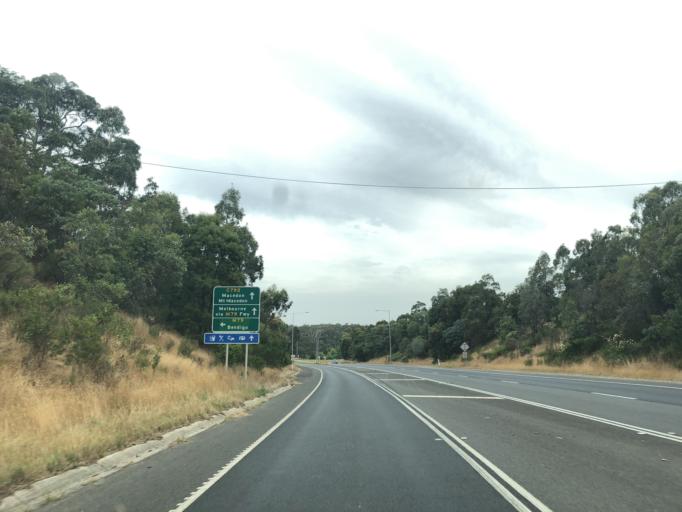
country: AU
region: Victoria
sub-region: Hume
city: Sunbury
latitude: -37.4110
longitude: 144.5409
